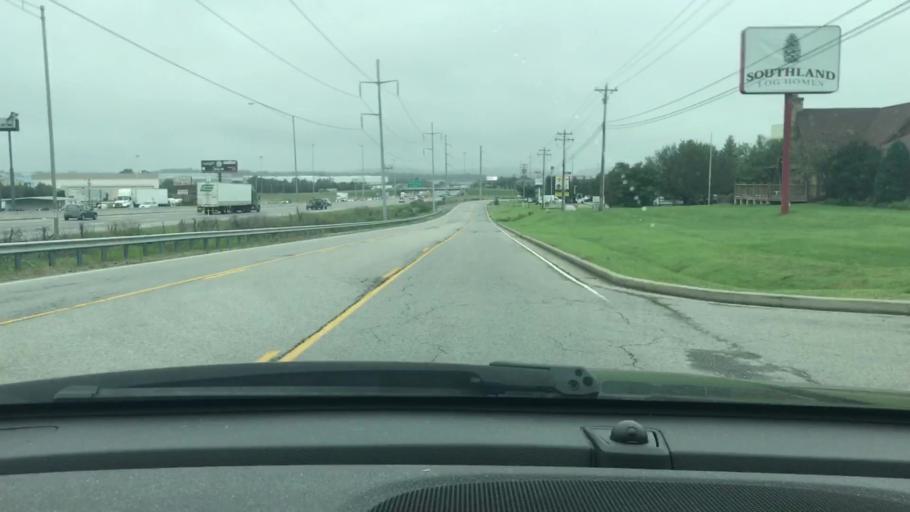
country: US
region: Tennessee
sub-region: Rutherford County
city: La Vergne
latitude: 35.9910
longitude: -86.5891
